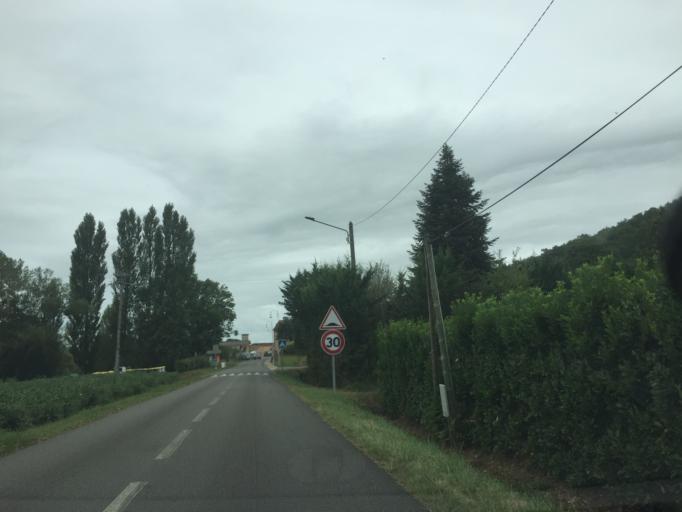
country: FR
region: Midi-Pyrenees
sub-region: Departement des Hautes-Pyrenees
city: Rabastens-de-Bigorre
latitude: 43.3737
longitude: 0.2140
